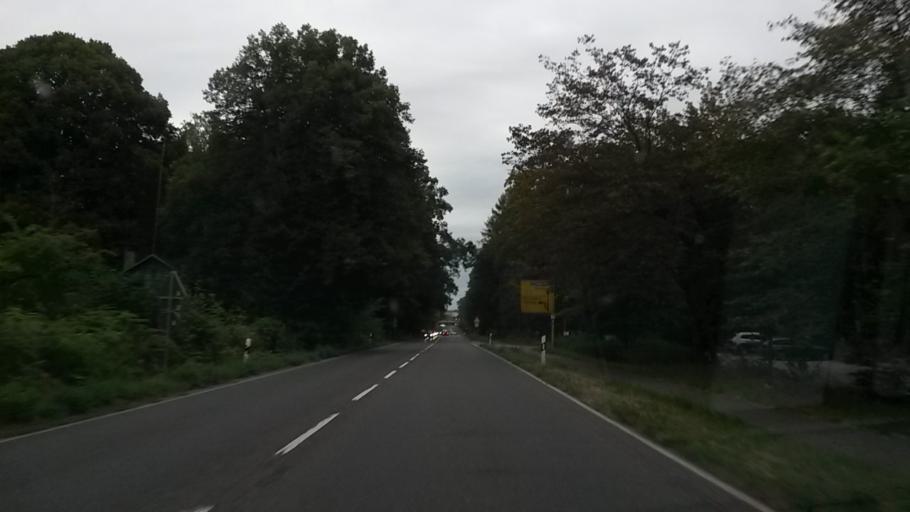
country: DE
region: North Rhine-Westphalia
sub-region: Regierungsbezirk Koln
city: Rath
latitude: 50.9430
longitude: 7.1161
